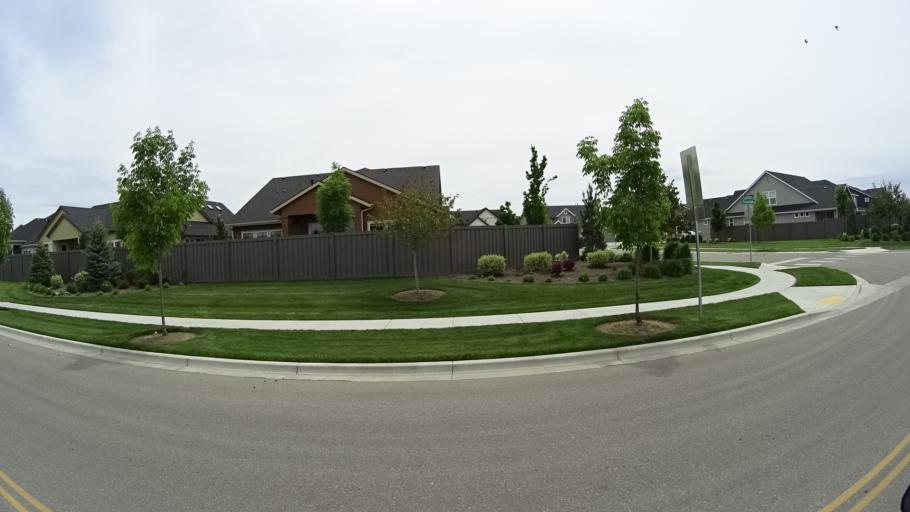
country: US
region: Idaho
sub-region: Ada County
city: Meridian
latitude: 43.5563
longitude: -116.3473
